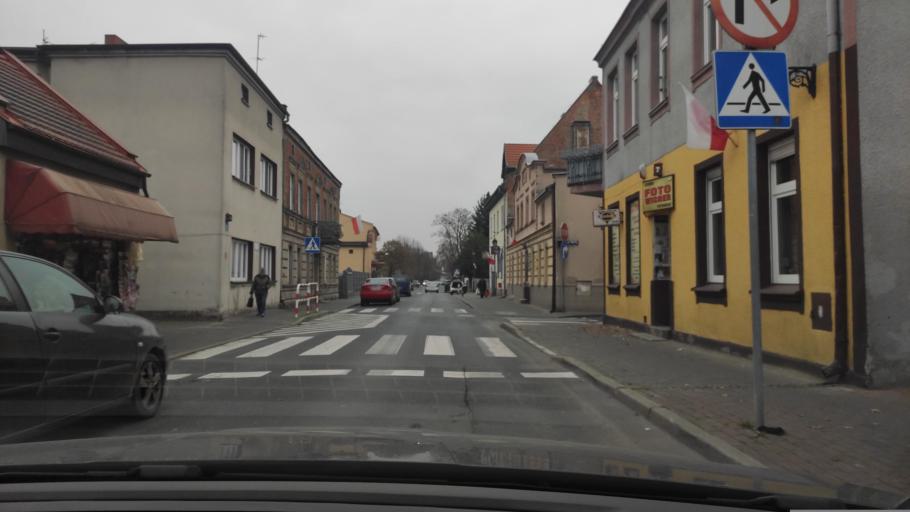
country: PL
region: Greater Poland Voivodeship
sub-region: Powiat poznanski
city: Kostrzyn
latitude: 52.3972
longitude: 17.2262
